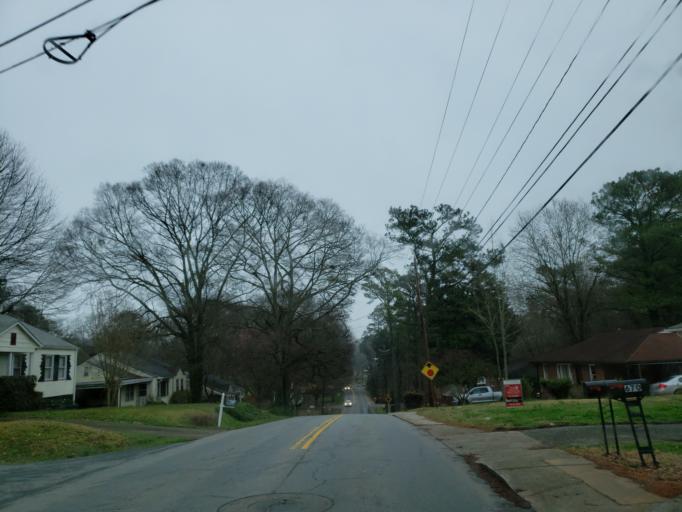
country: US
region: Georgia
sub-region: Cobb County
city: Fair Oaks
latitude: 33.9019
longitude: -84.5345
